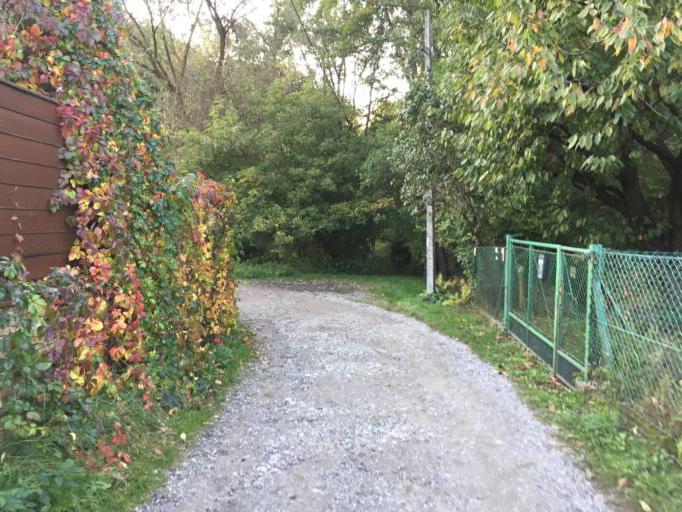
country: PL
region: Lesser Poland Voivodeship
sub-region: Powiat krakowski
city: Ochojno
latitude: 50.0182
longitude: 19.9976
